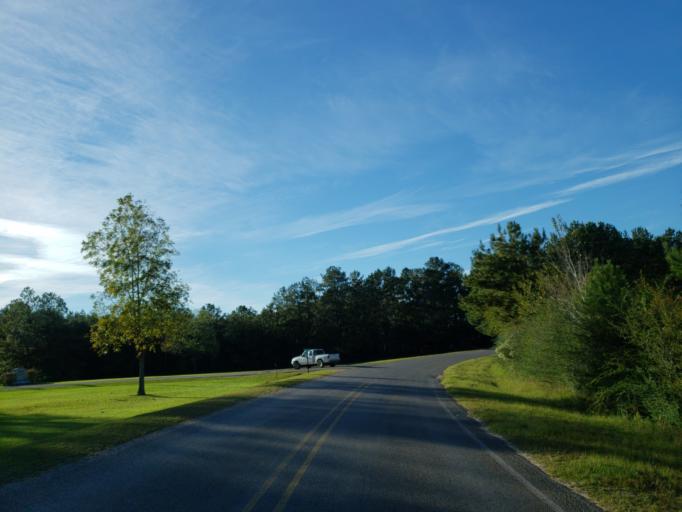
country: US
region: Mississippi
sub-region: Perry County
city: Richton
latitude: 31.3383
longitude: -88.8081
